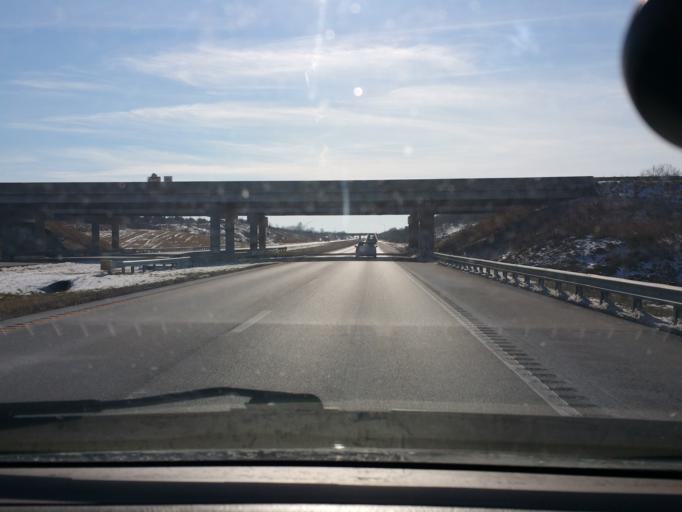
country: US
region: Missouri
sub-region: Clinton County
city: Cameron
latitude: 39.7545
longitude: -94.2200
